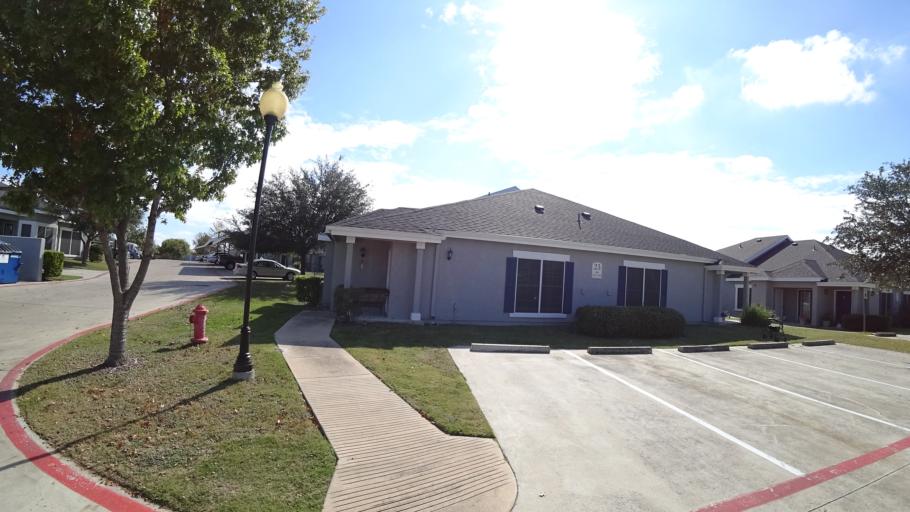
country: US
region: Texas
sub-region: Travis County
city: Windemere
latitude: 30.4547
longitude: -97.6389
